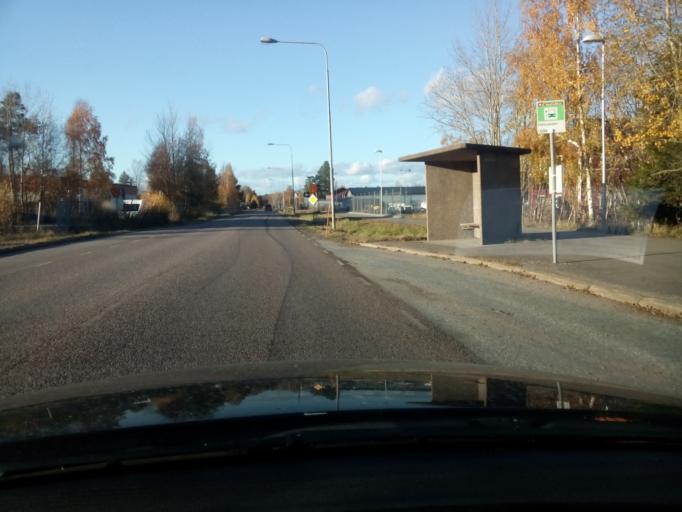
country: SE
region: Soedermanland
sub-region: Nykopings Kommun
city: Nykoping
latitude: 58.7182
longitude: 17.0276
